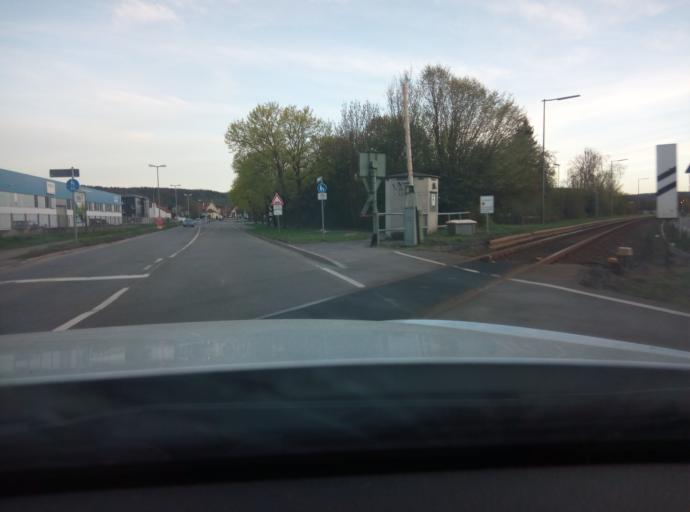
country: DE
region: Baden-Wuerttemberg
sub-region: Tuebingen Region
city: Tuebingen
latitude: 48.4983
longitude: 9.0313
